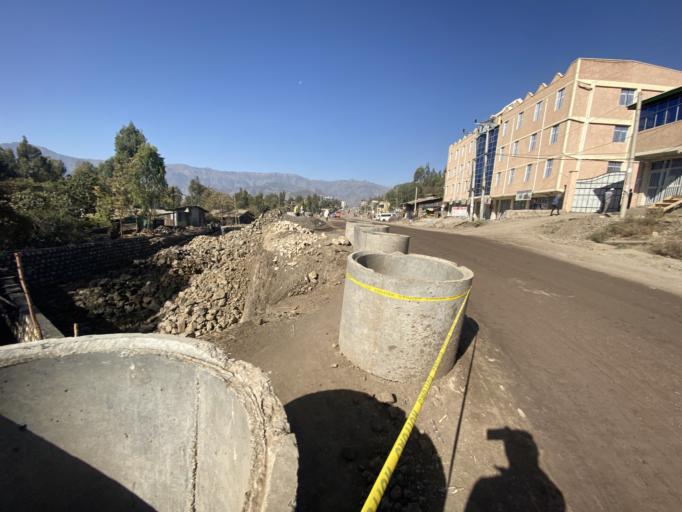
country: ET
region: Amhara
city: Robit
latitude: 11.8256
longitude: 39.5868
